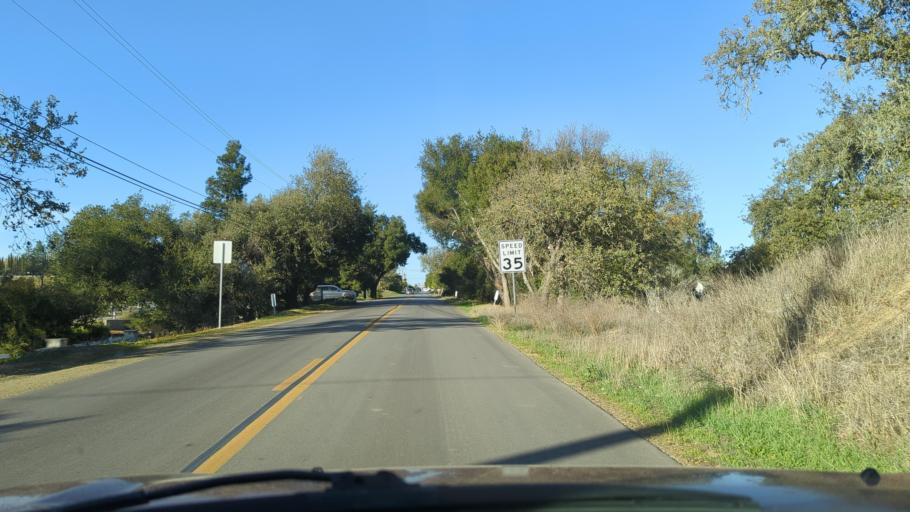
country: US
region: California
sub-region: Santa Barbara County
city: Santa Ynez
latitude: 34.6007
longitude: -120.0983
